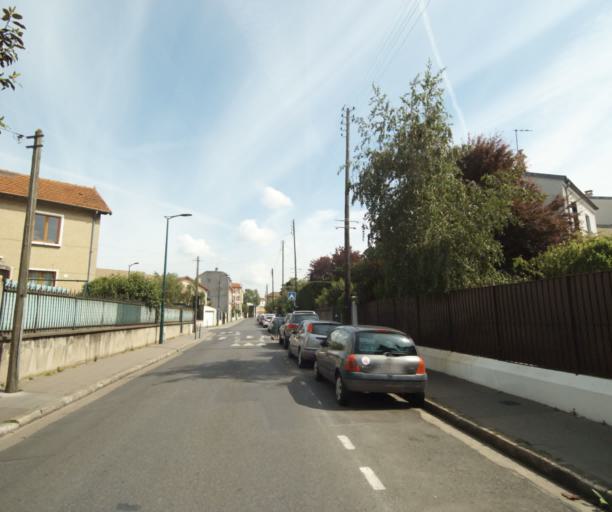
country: FR
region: Ile-de-France
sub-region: Departement des Hauts-de-Seine
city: La Garenne-Colombes
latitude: 48.9149
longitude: 2.2420
